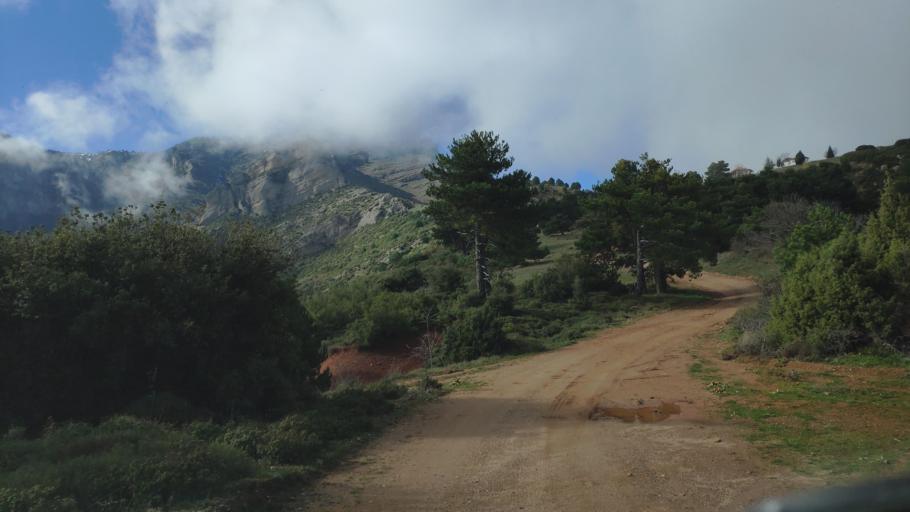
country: GR
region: West Greece
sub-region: Nomos Achaias
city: Aiyira
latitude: 38.0565
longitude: 22.4440
